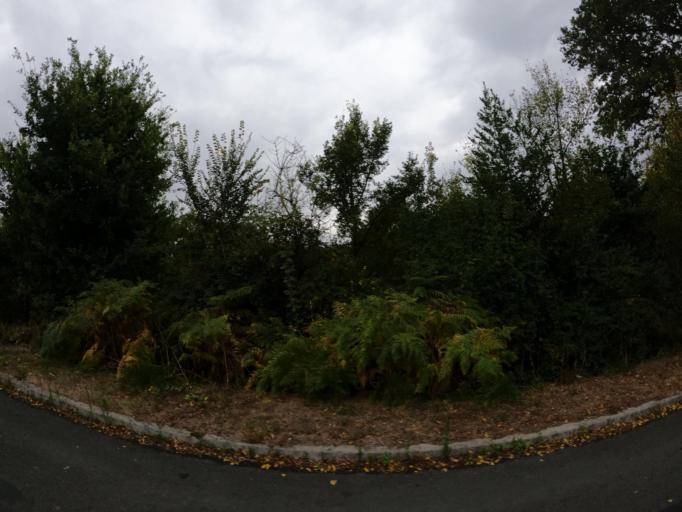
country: FR
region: Pays de la Loire
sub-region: Departement de la Vendee
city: Montaigu
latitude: 46.9729
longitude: -1.2870
